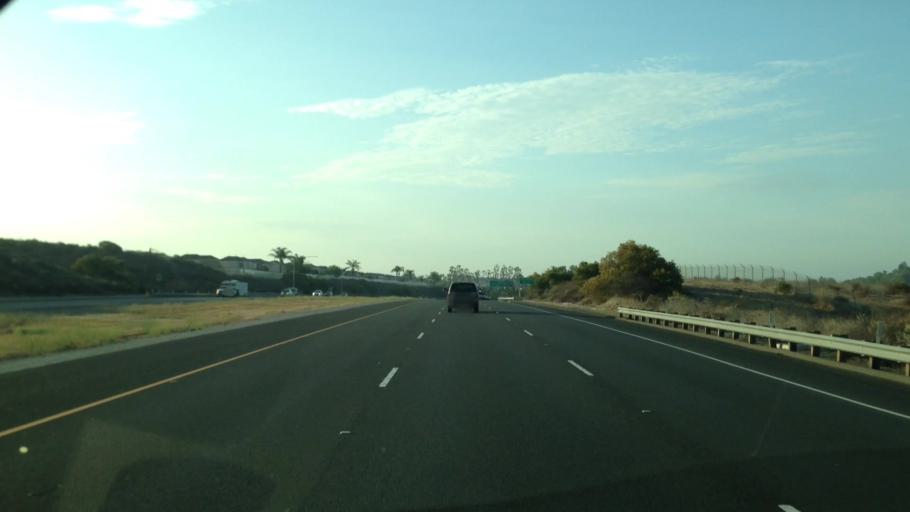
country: US
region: California
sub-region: Orange County
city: Foothill Ranch
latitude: 33.6869
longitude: -117.6803
